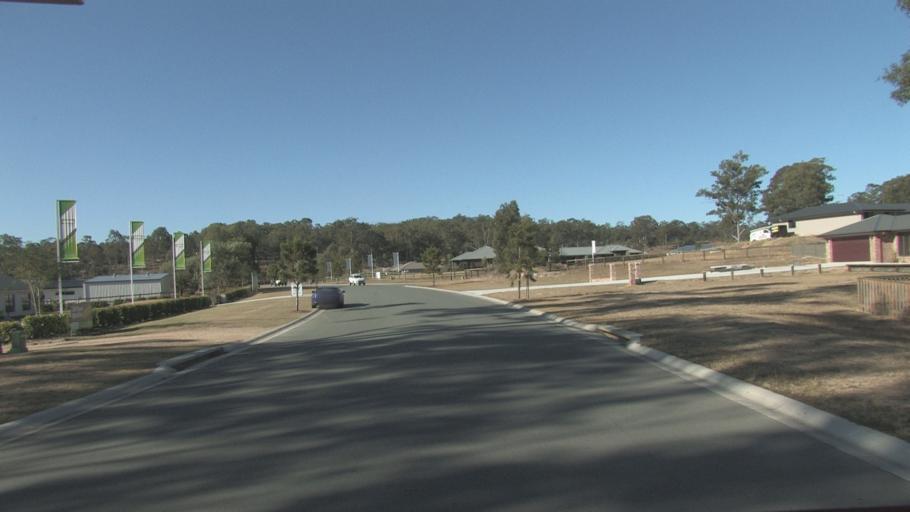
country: AU
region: Queensland
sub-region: Logan
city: Cedar Vale
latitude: -27.8669
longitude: 153.0562
